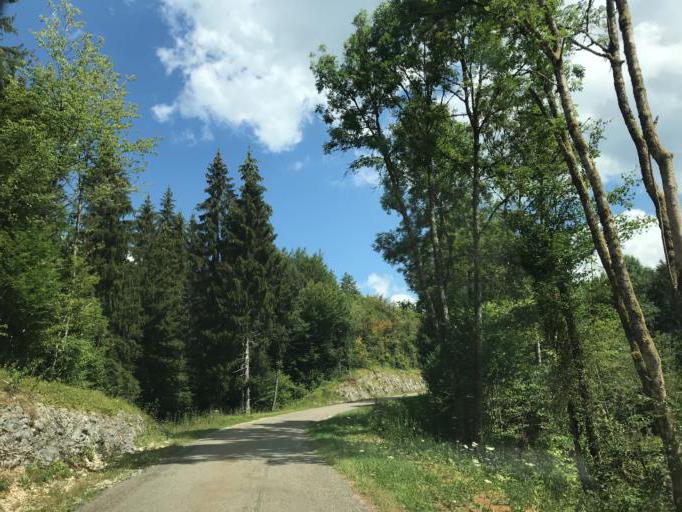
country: FR
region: Franche-Comte
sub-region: Departement du Jura
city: Moirans-en-Montagne
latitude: 46.4963
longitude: 5.7782
